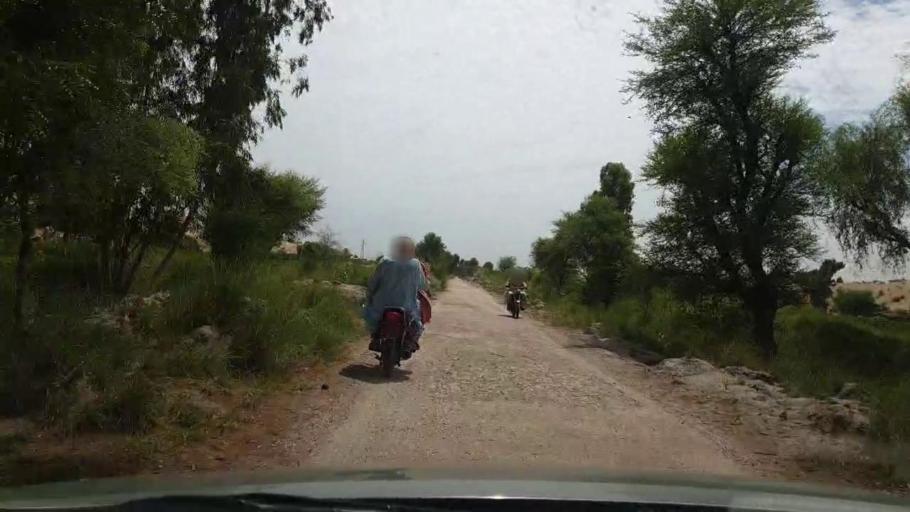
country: PK
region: Sindh
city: Bozdar
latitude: 27.0706
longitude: 68.9682
